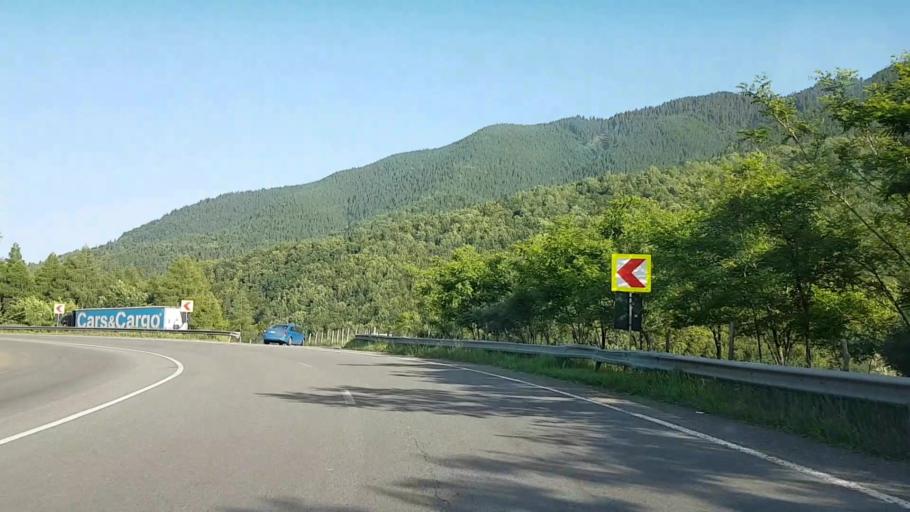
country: RO
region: Bistrita-Nasaud
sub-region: Comuna Tiha Bargaului
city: Tureac
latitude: 47.2219
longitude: 24.9298
